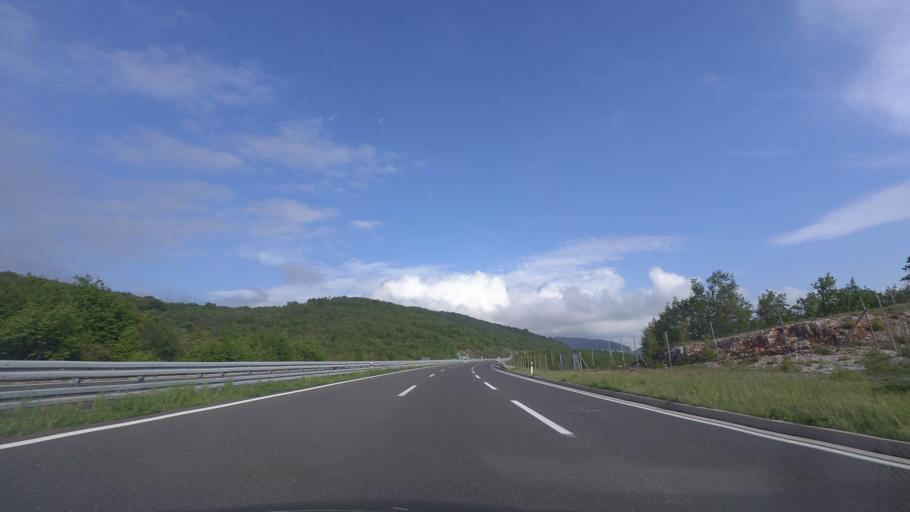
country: HR
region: Primorsko-Goranska
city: Krasica
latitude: 45.3609
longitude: 14.5737
